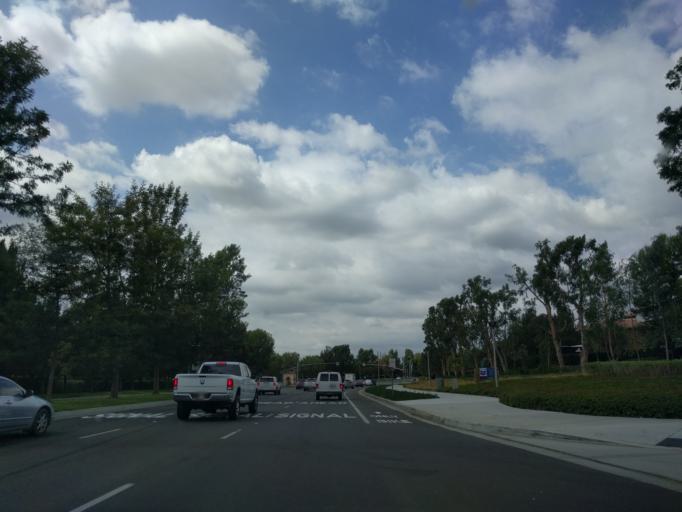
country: US
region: California
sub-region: Orange County
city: North Tustin
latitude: 33.7333
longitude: -117.7613
